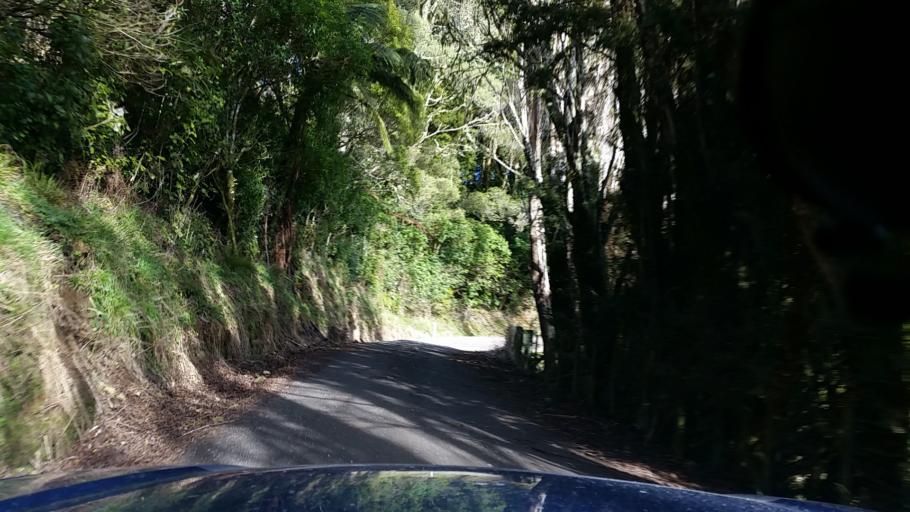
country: NZ
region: Taranaki
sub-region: New Plymouth District
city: Waitara
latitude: -39.0321
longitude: 174.7895
